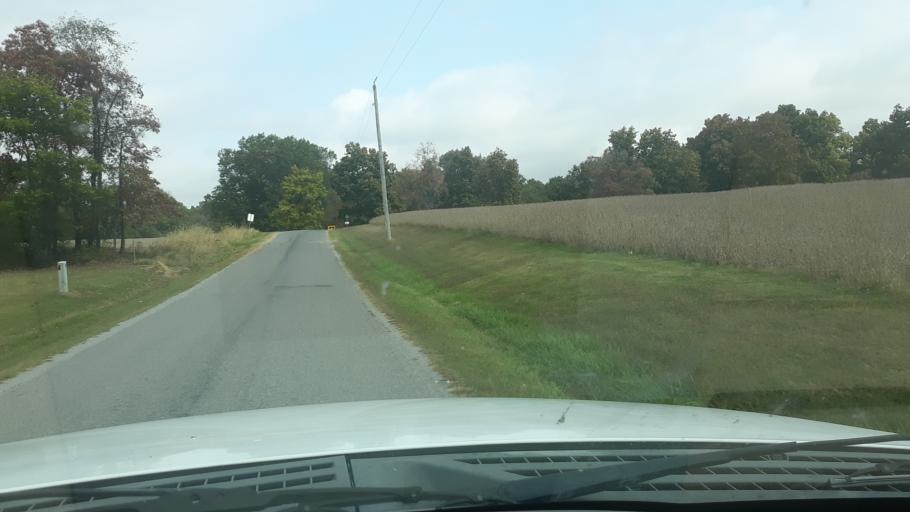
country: US
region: Illinois
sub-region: Saline County
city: Eldorado
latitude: 37.8353
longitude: -88.4849
